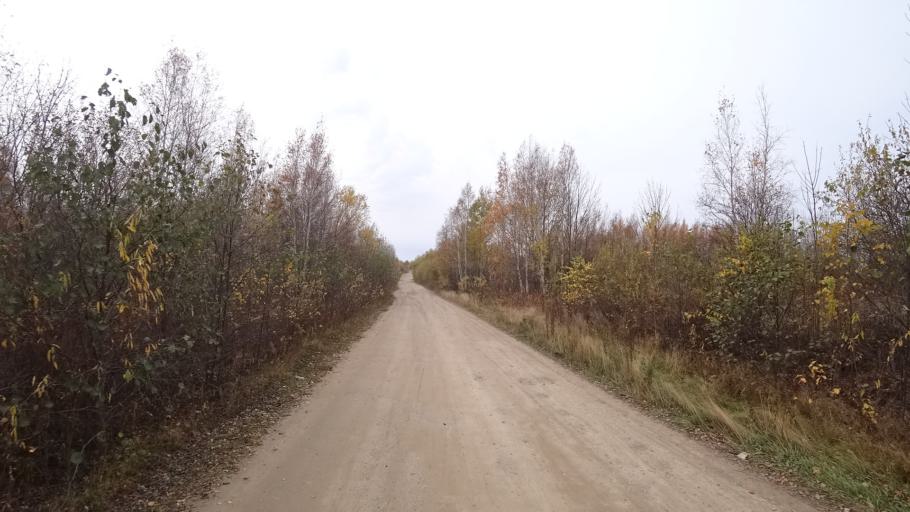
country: RU
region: Khabarovsk Krai
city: Amursk
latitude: 50.1427
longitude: 136.9631
